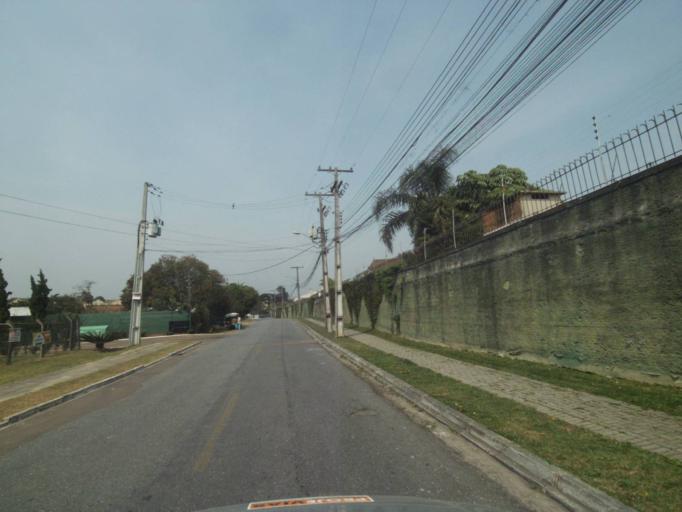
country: BR
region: Parana
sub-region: Pinhais
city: Pinhais
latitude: -25.4797
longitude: -49.2178
